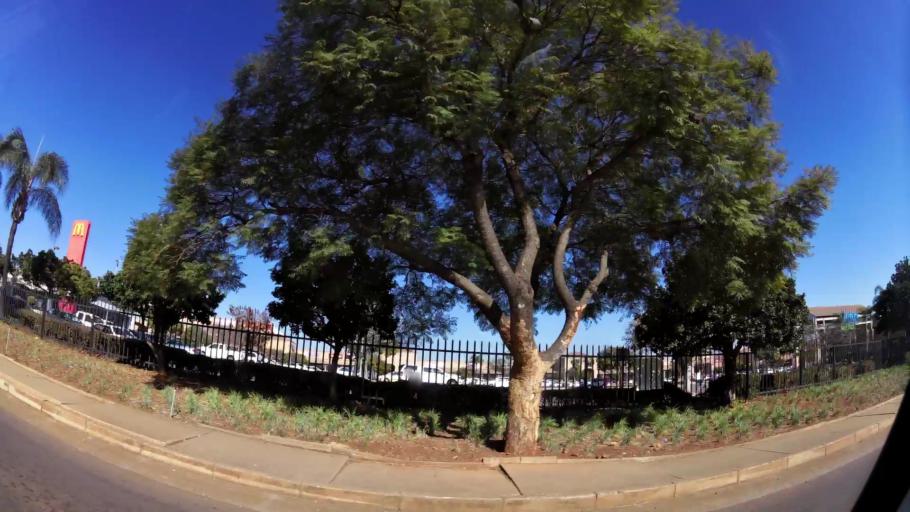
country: ZA
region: Gauteng
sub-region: City of Tshwane Metropolitan Municipality
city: Pretoria
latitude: -25.7877
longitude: 28.3082
